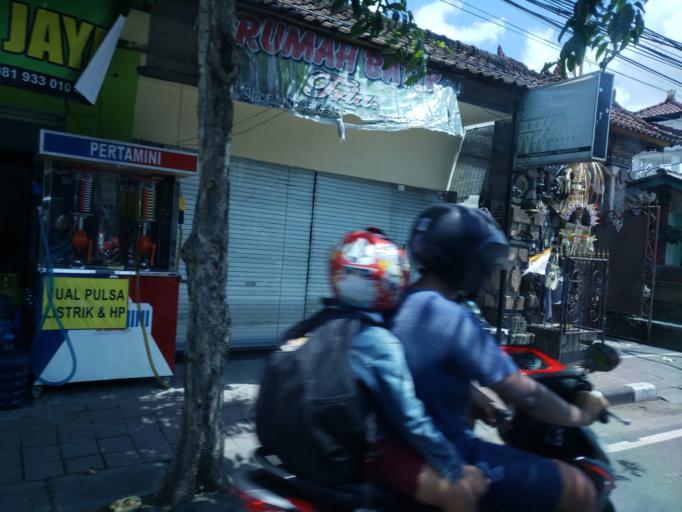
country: ID
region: Bali
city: Kelanabian
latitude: -8.7579
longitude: 115.1767
